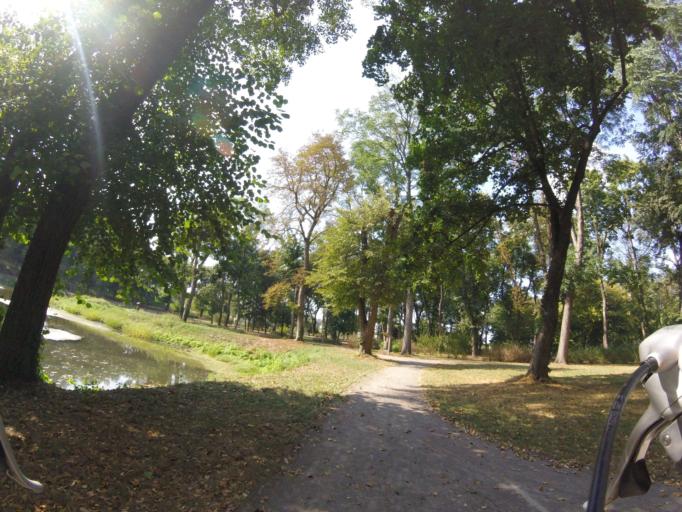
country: HU
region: Szabolcs-Szatmar-Bereg
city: Anarcs
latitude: 48.1749
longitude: 22.0954
